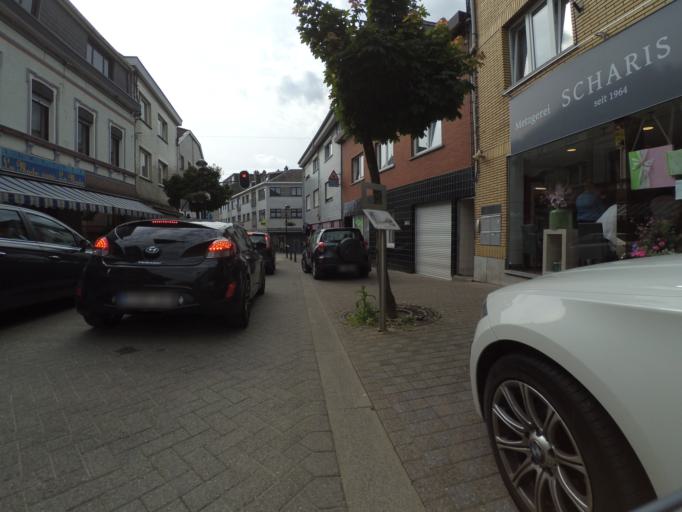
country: BE
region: Wallonia
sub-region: Province de Liege
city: La Calamine
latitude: 50.7166
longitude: 6.0113
